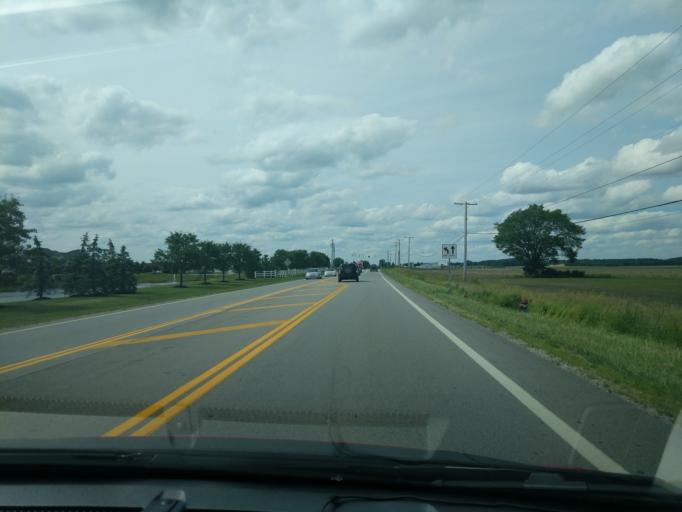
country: US
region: Ohio
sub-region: Union County
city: Marysville
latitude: 40.2670
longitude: -83.3747
